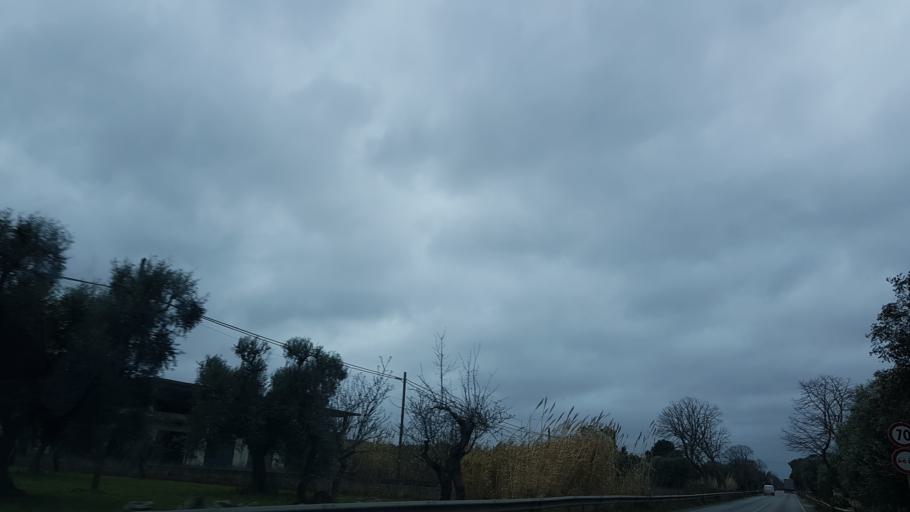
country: IT
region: Apulia
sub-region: Provincia di Brindisi
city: San Vito dei Normanni
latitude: 40.6567
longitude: 17.7344
